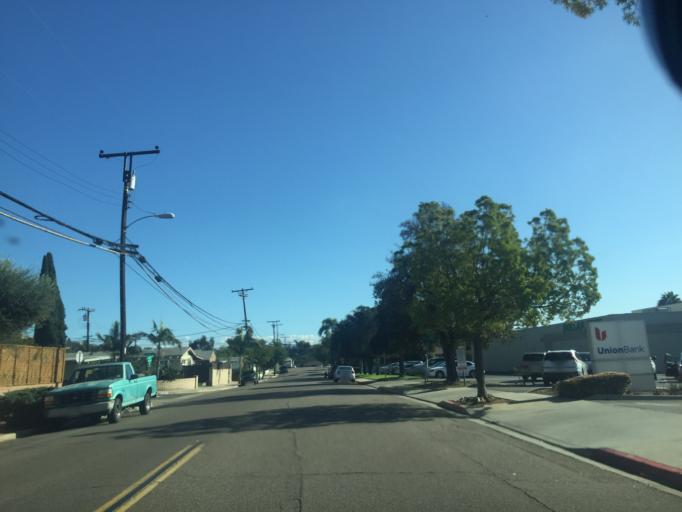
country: US
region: California
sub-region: San Diego County
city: La Mesa
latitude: 32.7925
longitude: -117.0803
